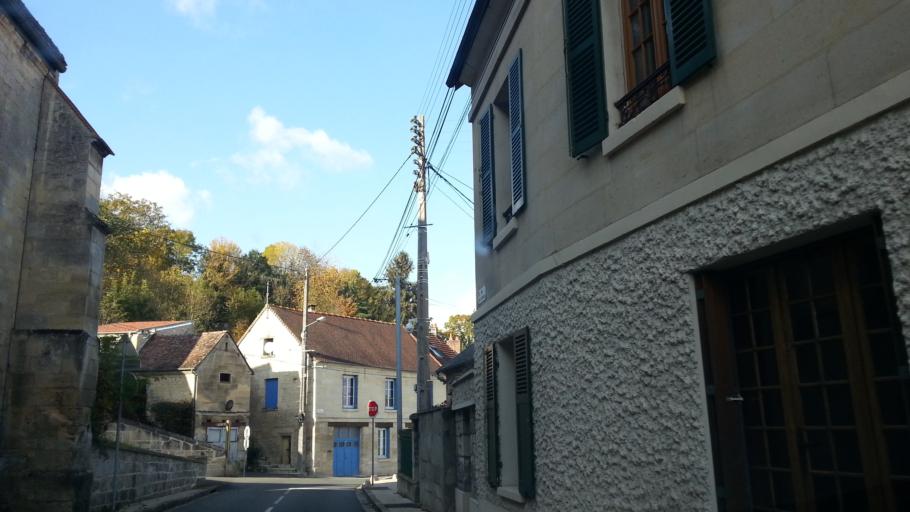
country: FR
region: Picardie
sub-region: Departement de l'Oise
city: Thiverny
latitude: 49.2551
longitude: 2.4011
